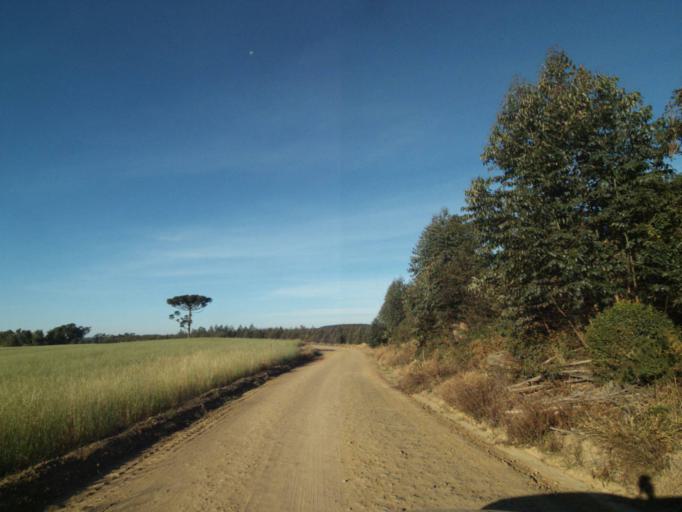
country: BR
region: Parana
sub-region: Tibagi
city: Tibagi
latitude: -24.5358
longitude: -50.6039
